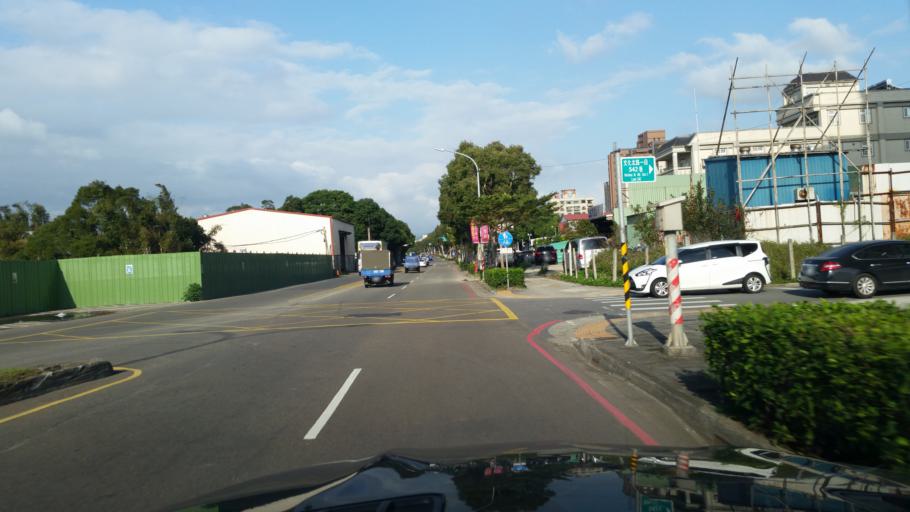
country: TW
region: Taiwan
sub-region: Taoyuan
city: Taoyuan
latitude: 25.0796
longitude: 121.3679
